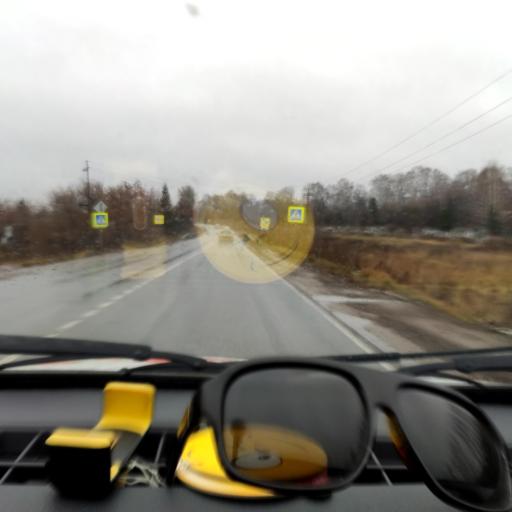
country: RU
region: Bashkortostan
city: Iglino
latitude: 54.7952
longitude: 56.3000
